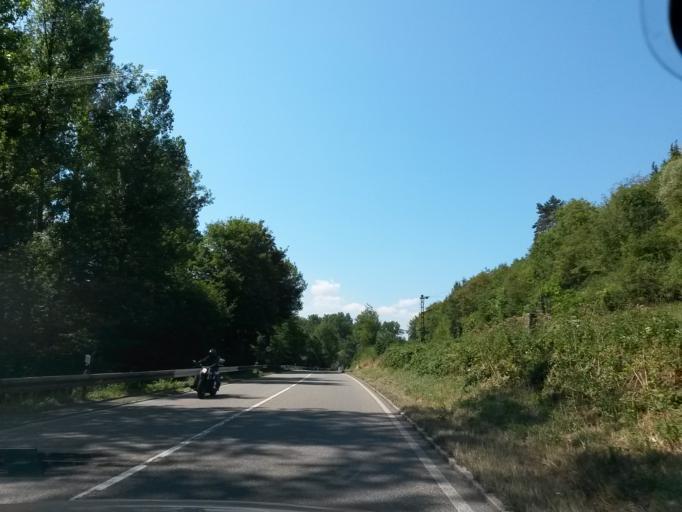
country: DE
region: Baden-Wuerttemberg
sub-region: Karlsruhe Region
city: Niefern-Oschelbronn
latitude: 48.9289
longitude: 8.7925
